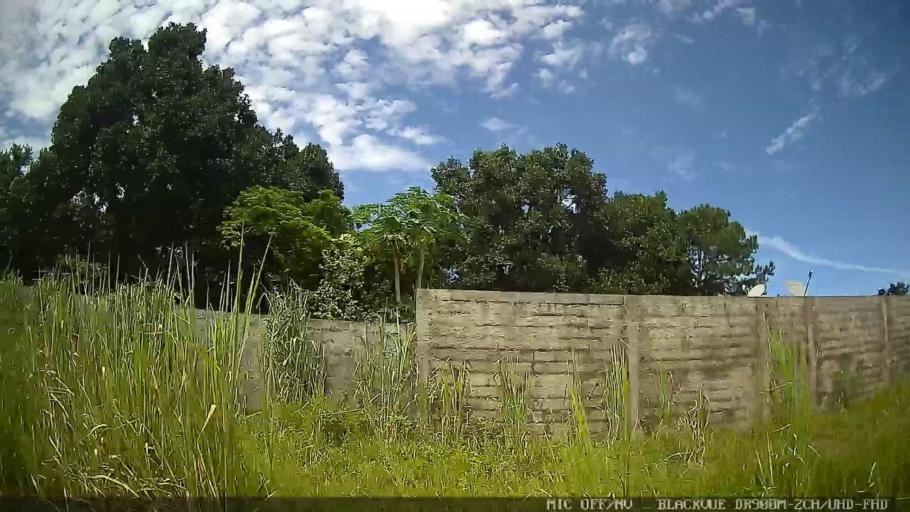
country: BR
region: Sao Paulo
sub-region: Iguape
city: Iguape
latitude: -24.7165
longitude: -47.5211
